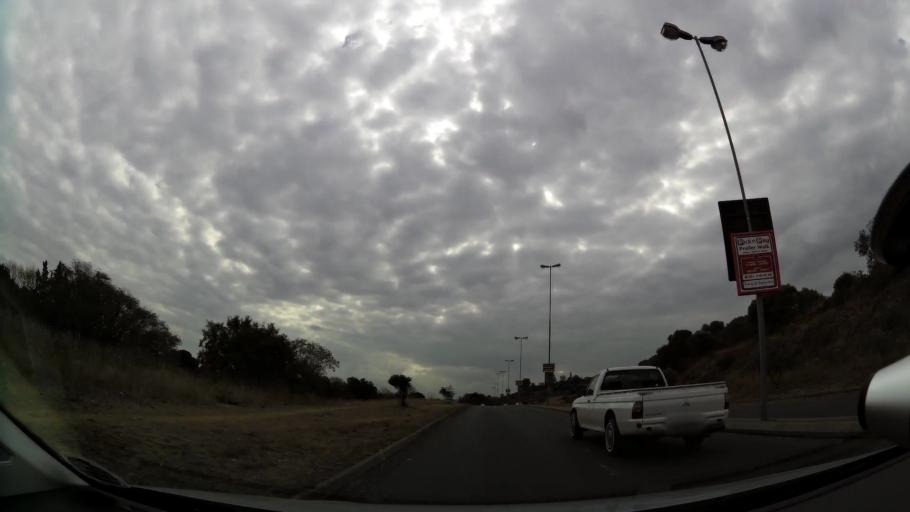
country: ZA
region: Orange Free State
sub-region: Mangaung Metropolitan Municipality
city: Bloemfontein
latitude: -29.1039
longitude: 26.2133
